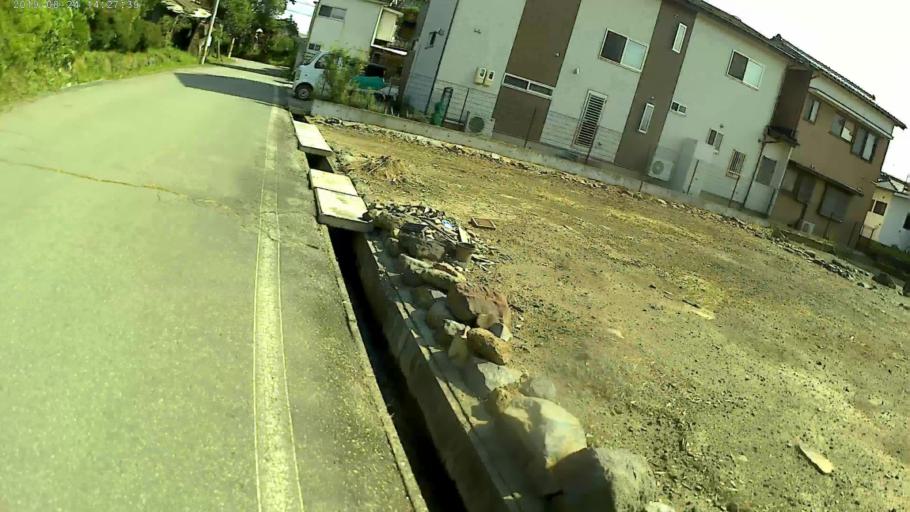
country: JP
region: Nagano
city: Komoro
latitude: 36.2682
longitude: 138.4322
